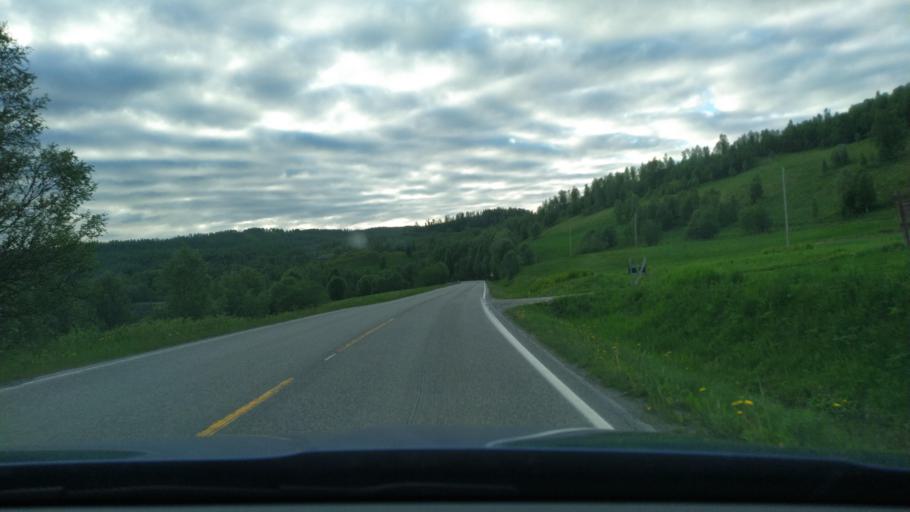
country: NO
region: Troms
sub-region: Sorreisa
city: Sorreisa
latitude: 69.0926
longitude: 18.3406
